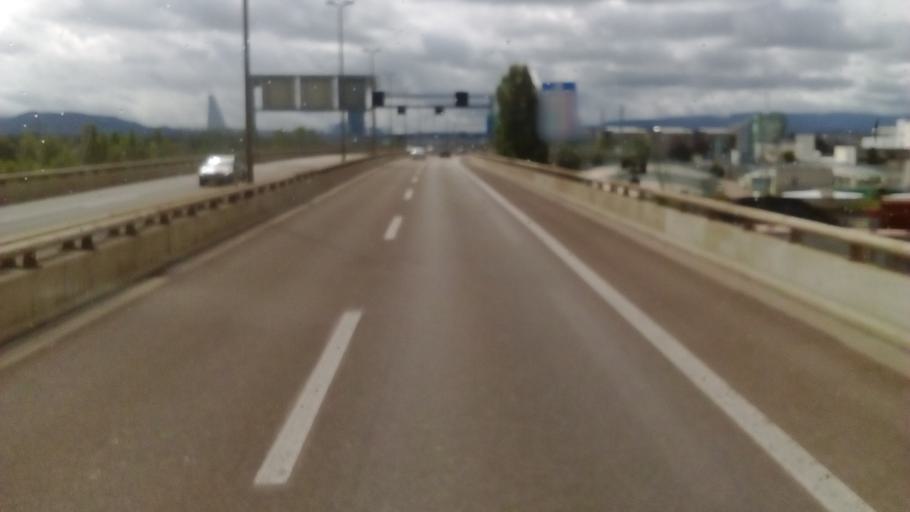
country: DE
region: Baden-Wuerttemberg
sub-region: Freiburg Region
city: Weil am Rhein
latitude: 47.5858
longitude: 7.6020
